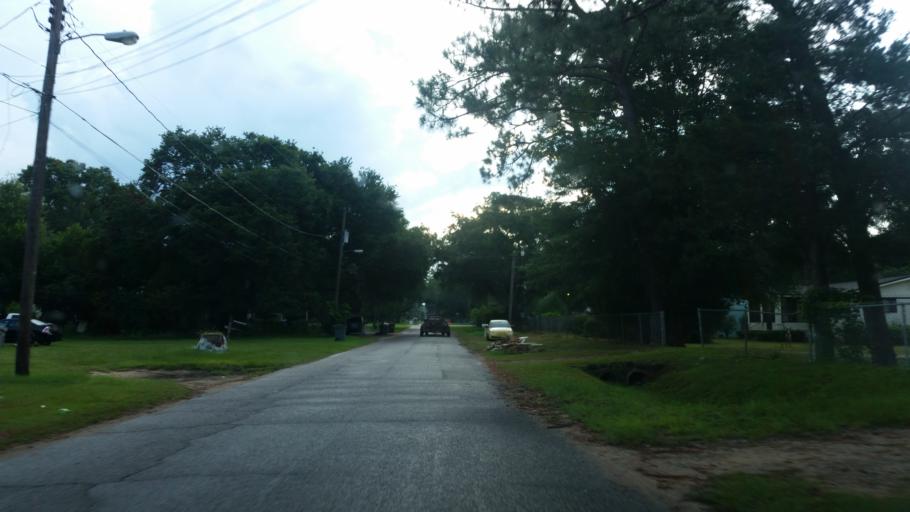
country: US
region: Florida
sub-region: Escambia County
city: Brent
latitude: 30.4575
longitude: -87.2469
